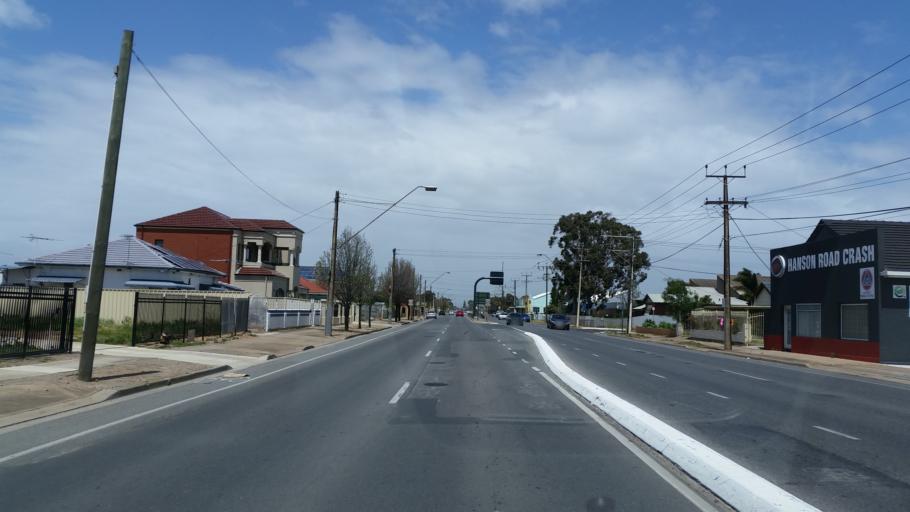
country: AU
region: South Australia
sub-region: Charles Sturt
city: Woodville North
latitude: -34.8517
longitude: 138.5468
